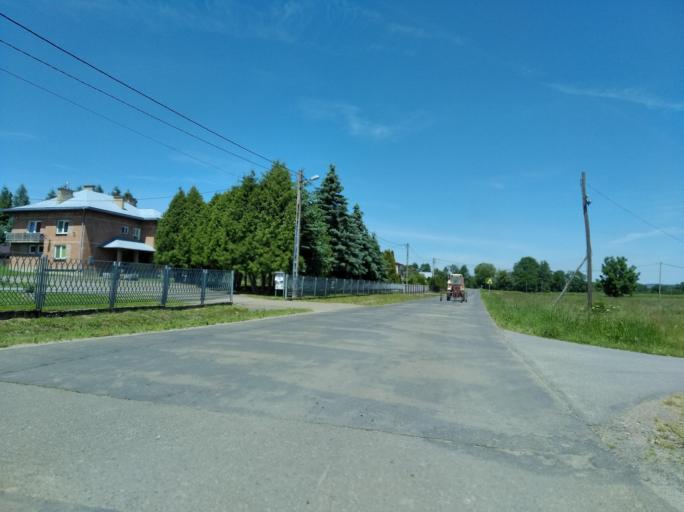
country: PL
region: Subcarpathian Voivodeship
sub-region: Powiat jasielski
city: Tarnowiec
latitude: 49.6999
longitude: 21.5529
